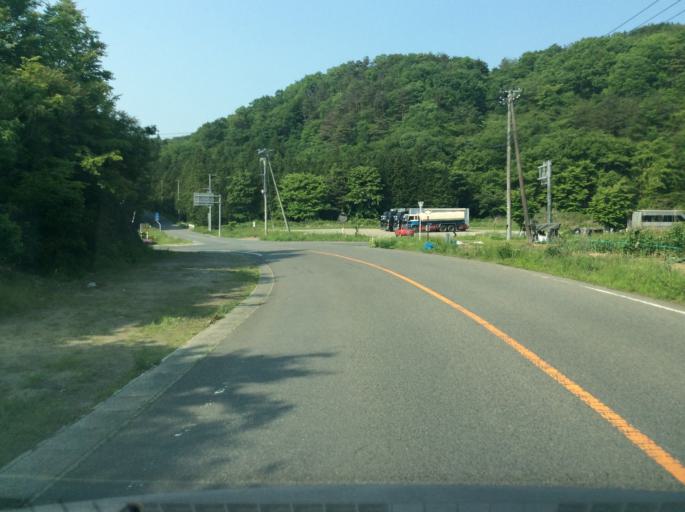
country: JP
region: Tochigi
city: Kuroiso
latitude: 37.0809
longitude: 140.2238
